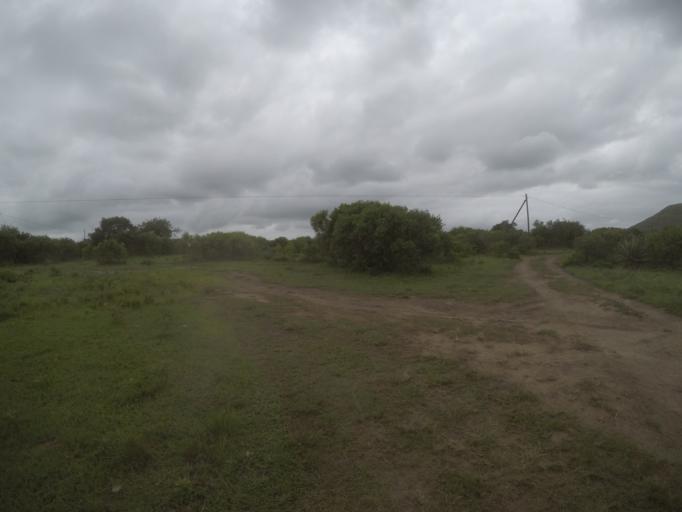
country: ZA
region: KwaZulu-Natal
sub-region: uThungulu District Municipality
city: Empangeni
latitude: -28.5937
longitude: 31.8462
